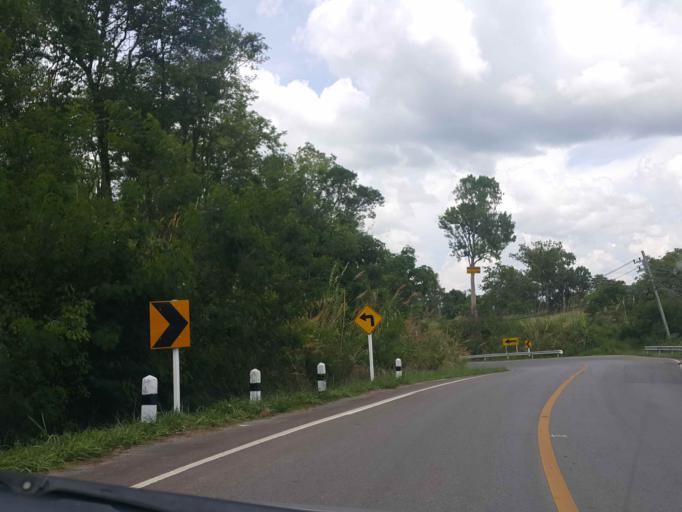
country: TH
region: Nan
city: Ban Luang
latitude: 18.8757
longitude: 100.5705
